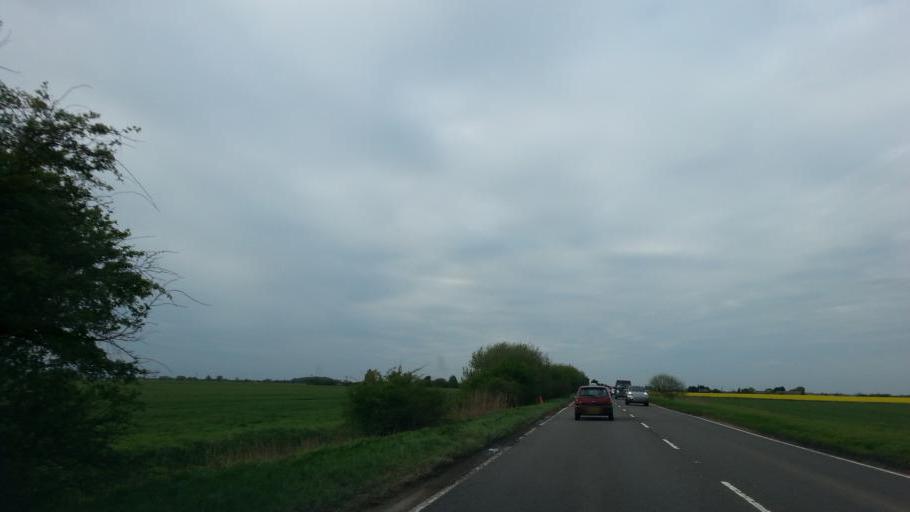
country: GB
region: England
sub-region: Cambridgeshire
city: March
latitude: 52.5782
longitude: 0.0562
